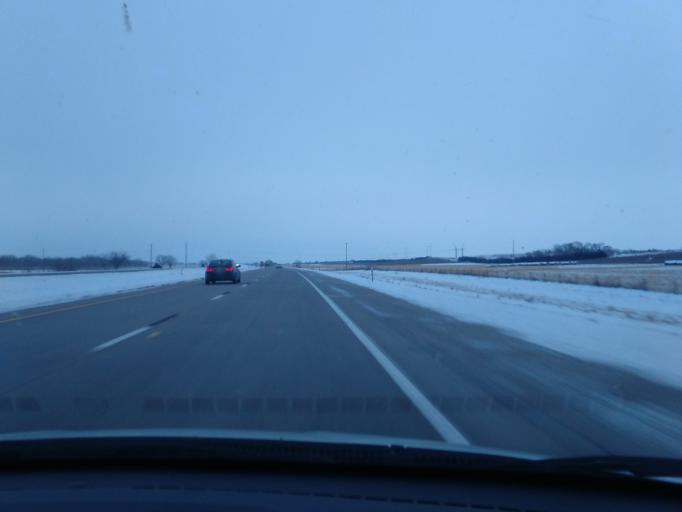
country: US
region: Nebraska
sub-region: Lincoln County
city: Sutherland
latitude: 41.1075
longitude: -101.3880
